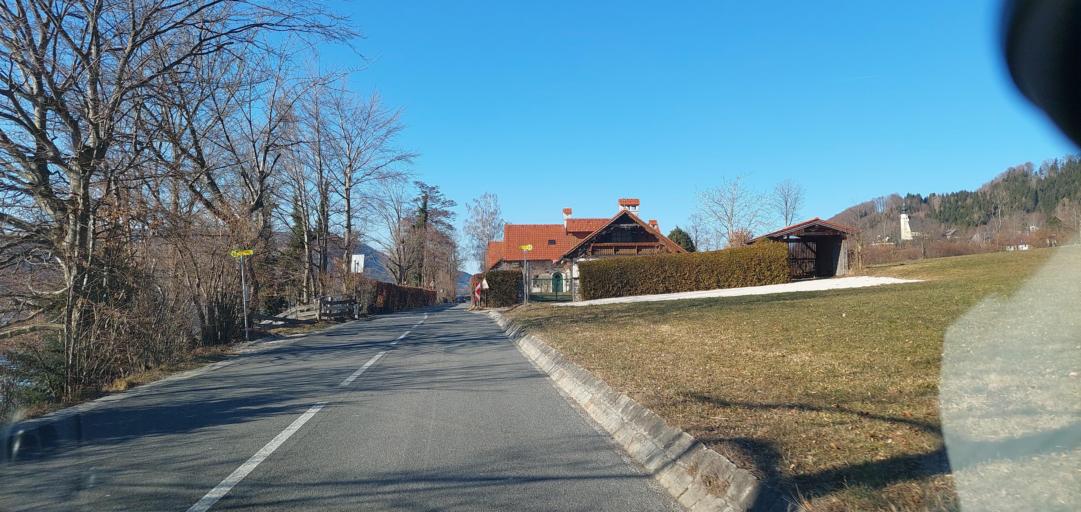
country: AT
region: Upper Austria
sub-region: Politischer Bezirk Vocklabruck
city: Steinbach am Attersee
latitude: 47.8258
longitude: 13.5472
